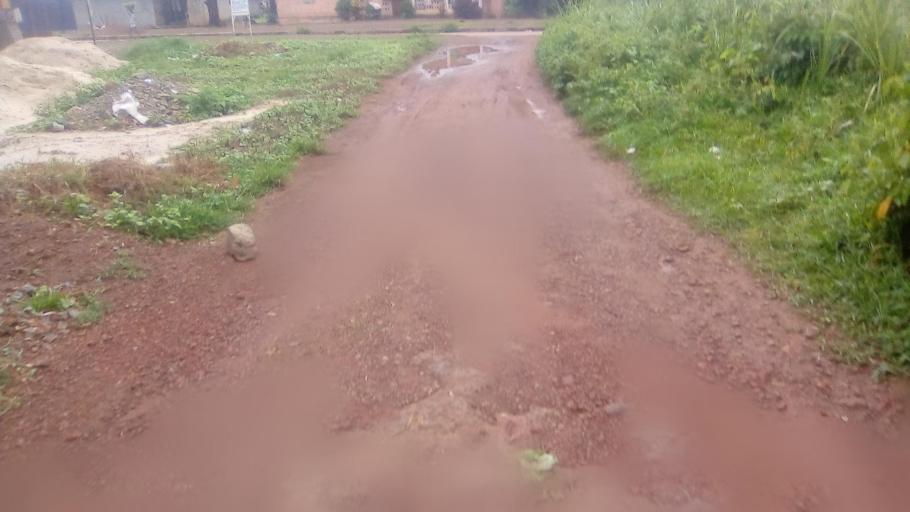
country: SL
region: Southern Province
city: Moyamba
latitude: 8.1508
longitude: -12.4326
